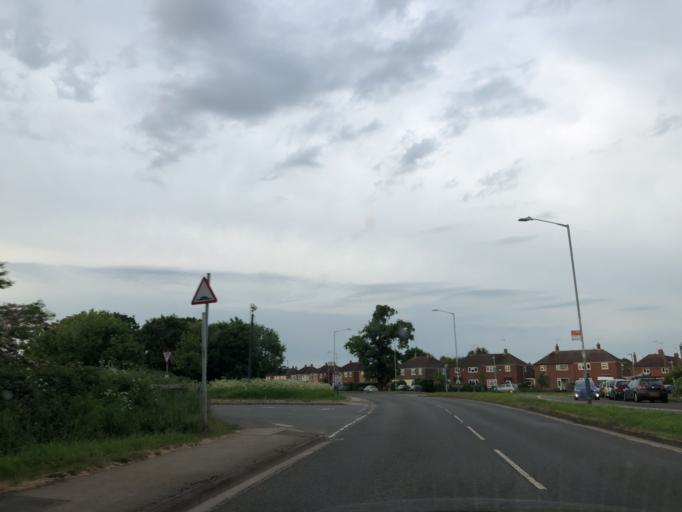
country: GB
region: England
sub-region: Warwickshire
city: Warwick
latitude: 52.2739
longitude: -1.6041
